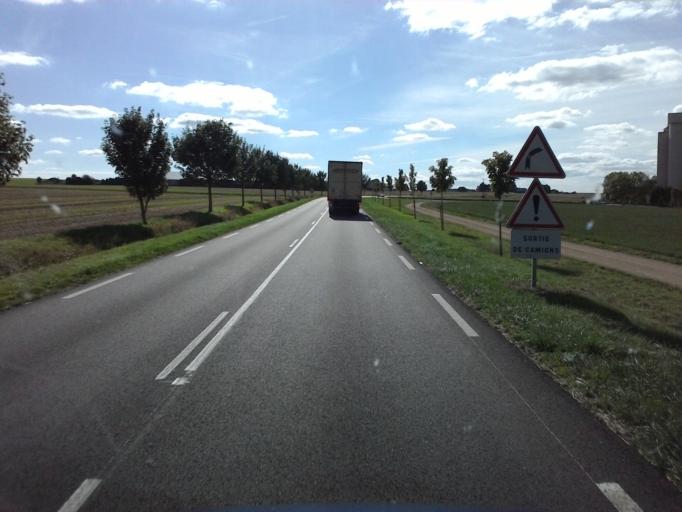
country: FR
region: Bourgogne
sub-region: Departement de la Cote-d'Or
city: Chatillon-sur-Seine
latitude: 47.7357
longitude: 4.4744
